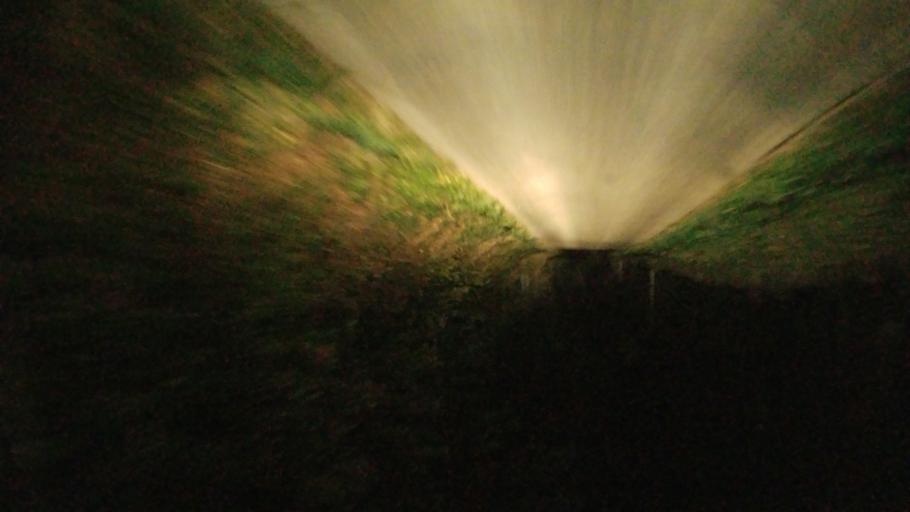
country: US
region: Ohio
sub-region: Ashland County
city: Loudonville
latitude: 40.7036
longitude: -82.1906
